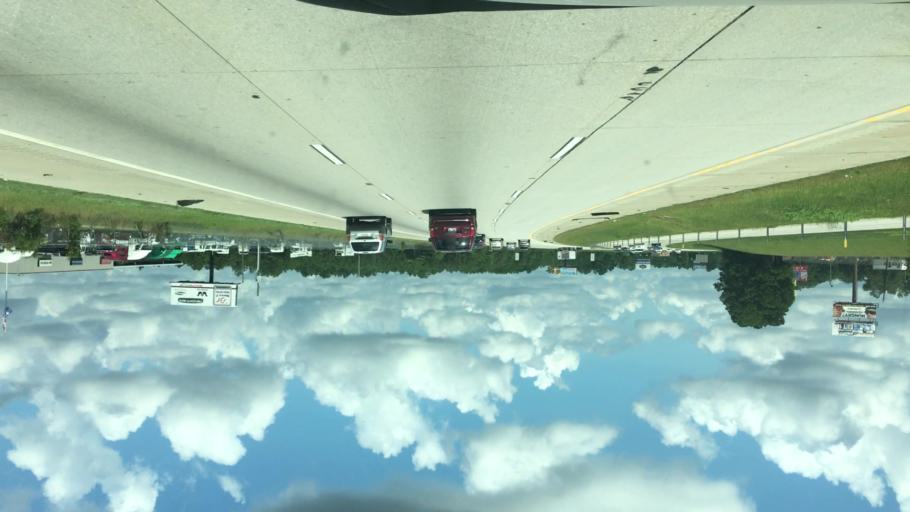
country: US
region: South Carolina
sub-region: Florence County
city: Florence
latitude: 34.2648
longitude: -79.7402
